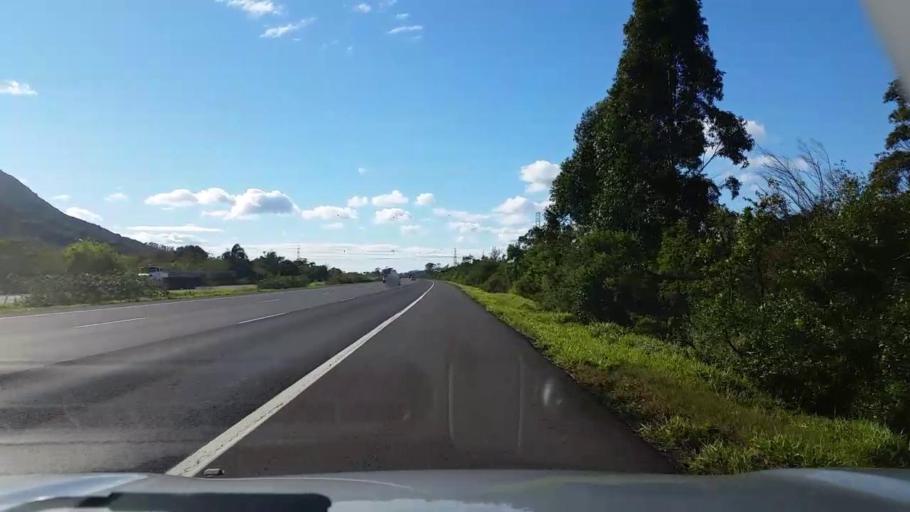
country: BR
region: Rio Grande do Sul
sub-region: Osorio
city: Osorio
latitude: -29.8980
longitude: -50.3200
